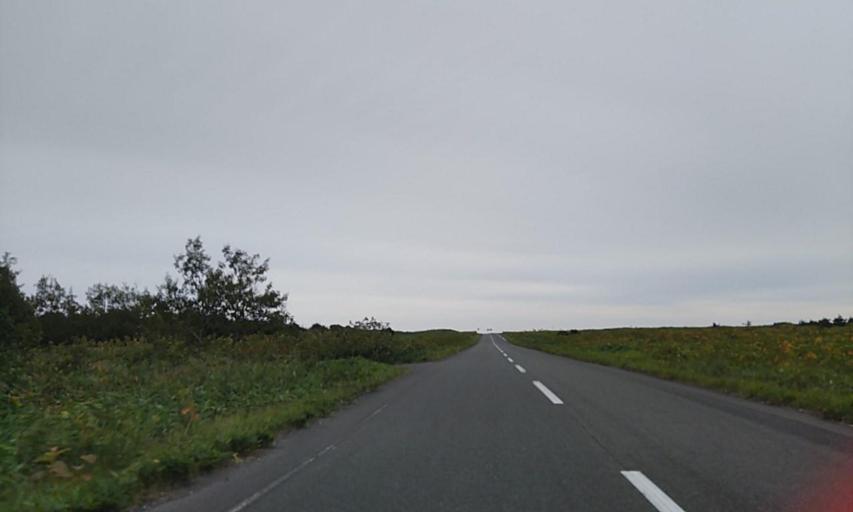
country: JP
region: Hokkaido
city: Makubetsu
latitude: 45.2675
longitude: 142.2345
